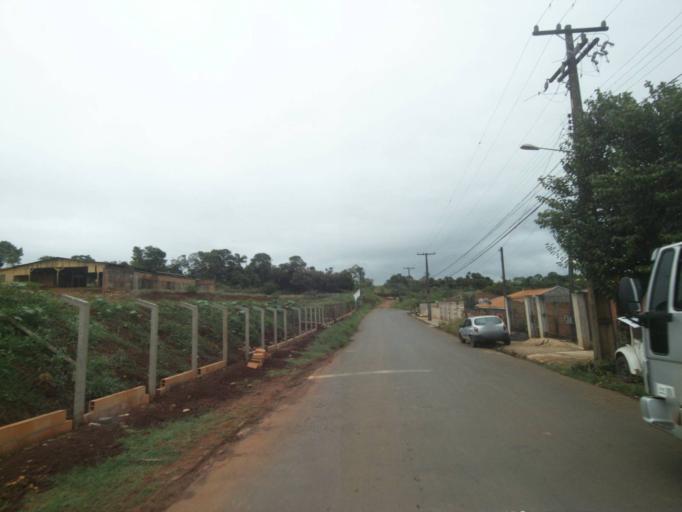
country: BR
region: Parana
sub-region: Telemaco Borba
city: Telemaco Borba
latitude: -24.3273
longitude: -50.6500
